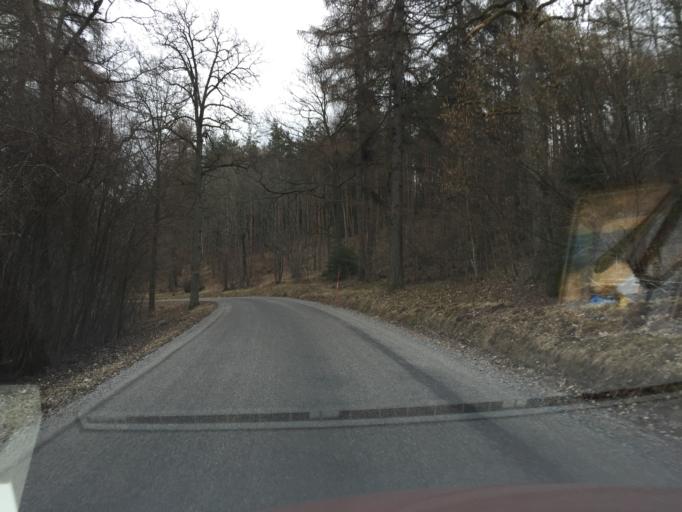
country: SE
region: Stockholm
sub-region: Botkyrka Kommun
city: Eriksberg
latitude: 59.2510
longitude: 17.7706
